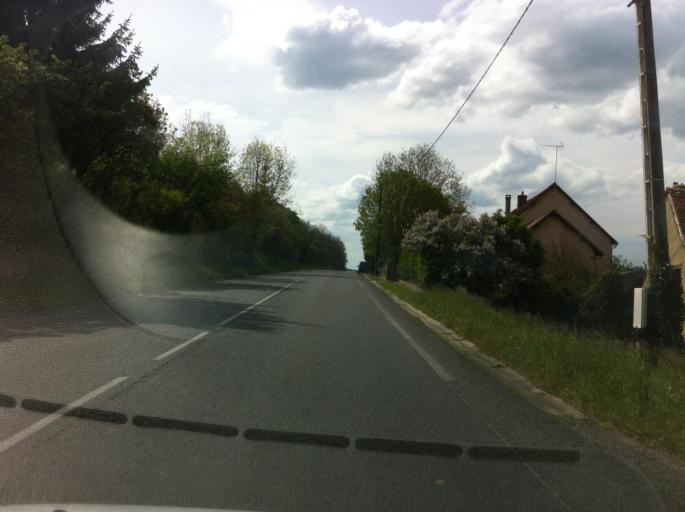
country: FR
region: Auvergne
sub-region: Departement de l'Allier
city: Saint-Pourcain-sur-Sioule
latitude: 46.3182
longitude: 3.2440
